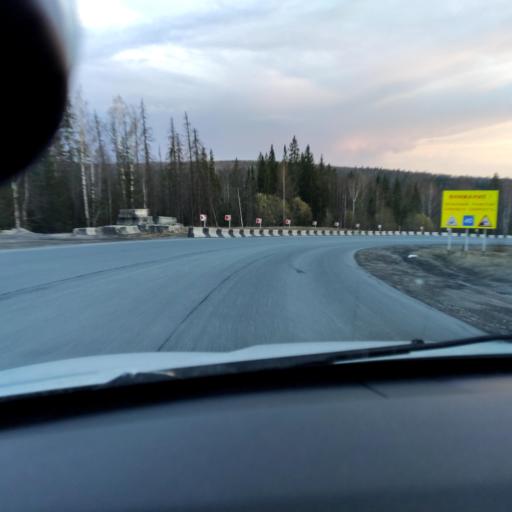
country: RU
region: Perm
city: Gremyachinsk
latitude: 58.4468
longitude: 57.8726
